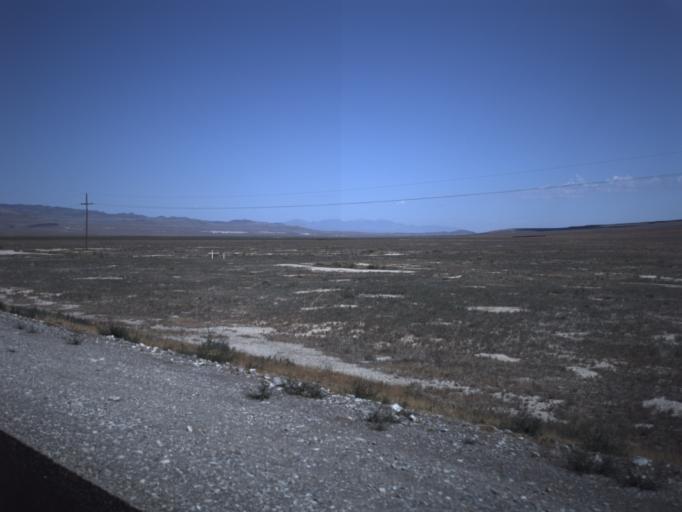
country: US
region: Utah
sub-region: Beaver County
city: Milford
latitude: 39.0650
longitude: -113.4474
